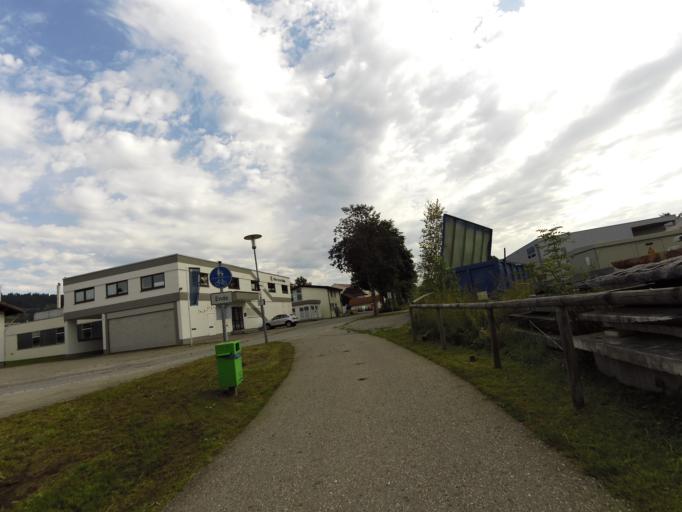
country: DE
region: Bavaria
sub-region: Swabia
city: Weiler-Simmerberg
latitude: 47.5854
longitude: 9.9191
